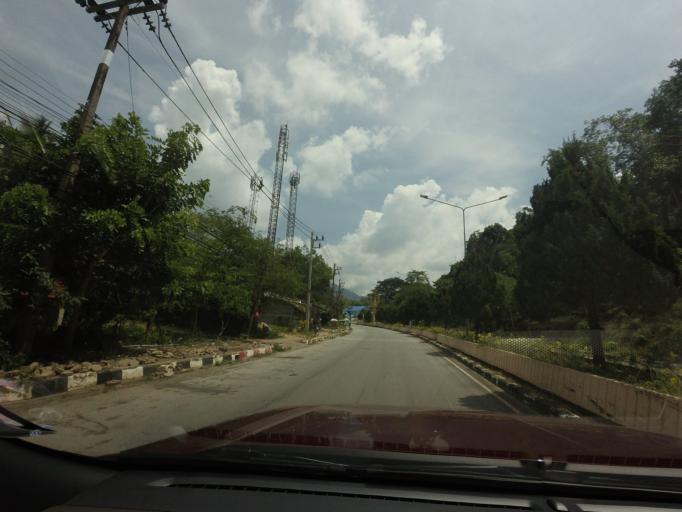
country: TH
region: Yala
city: Betong
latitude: 5.7677
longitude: 101.0543
